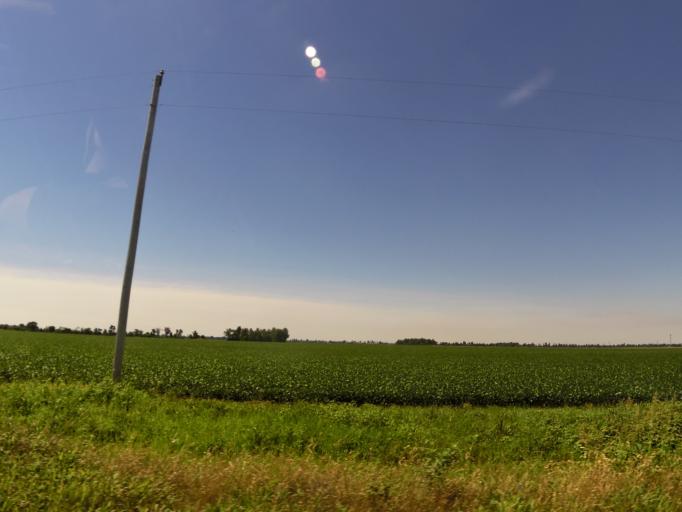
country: US
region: Missouri
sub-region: New Madrid County
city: Lilbourn
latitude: 36.5553
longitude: -89.6248
